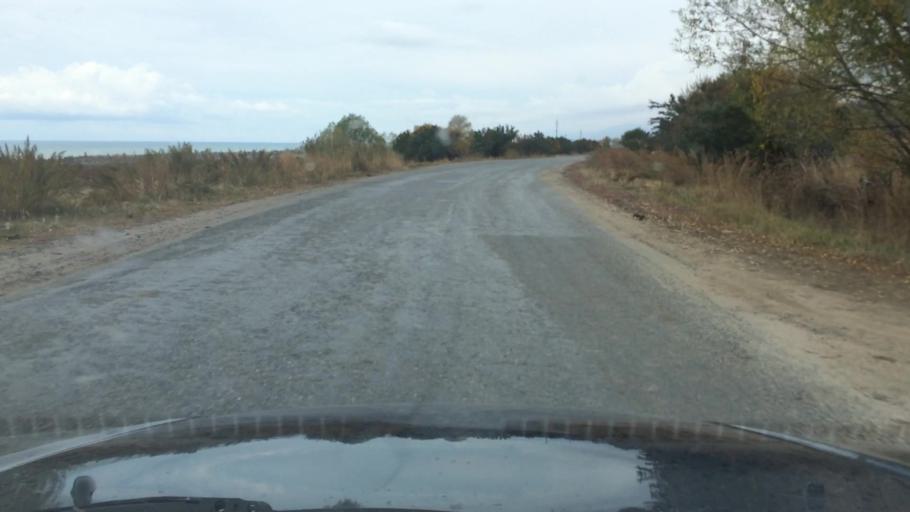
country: KG
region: Ysyk-Koel
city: Tyup
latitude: 42.7355
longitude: 77.9777
